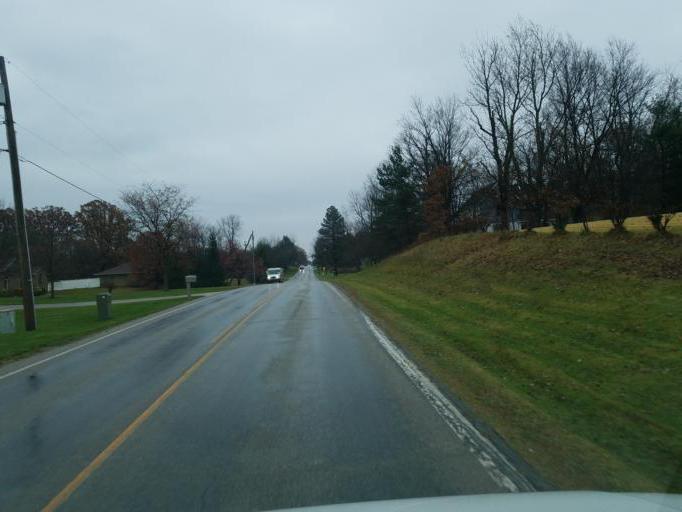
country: US
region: Ohio
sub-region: Richland County
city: Ontario
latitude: 40.7469
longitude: -82.6013
